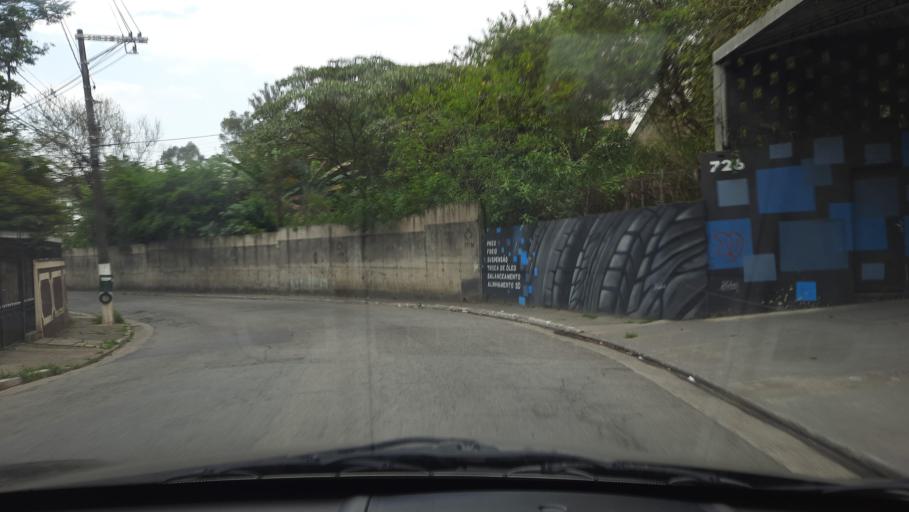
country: BR
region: Sao Paulo
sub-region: Caieiras
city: Caieiras
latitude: -23.4528
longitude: -46.7427
